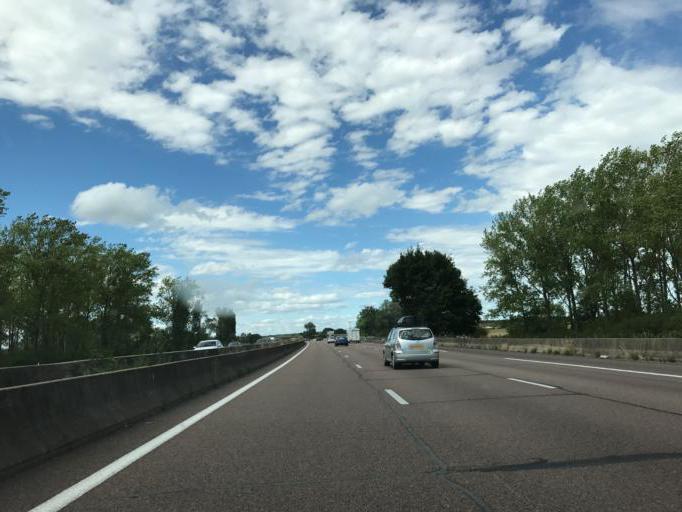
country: FR
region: Bourgogne
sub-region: Departement de Saone-et-Loire
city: Champforgeuil
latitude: 46.8334
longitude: 4.8322
